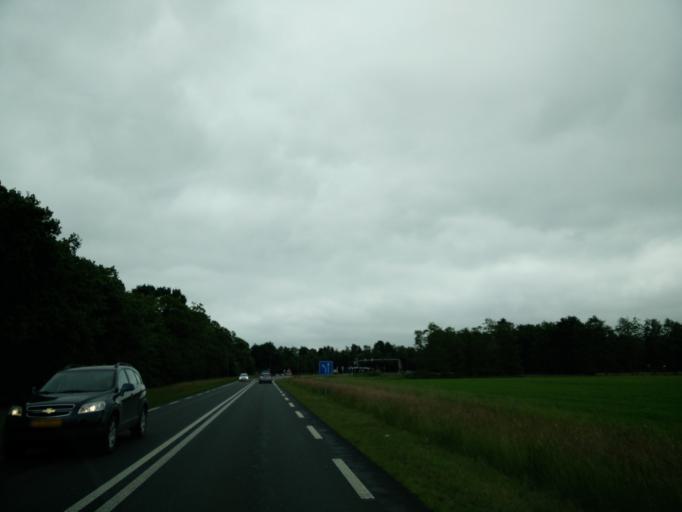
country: NL
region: Groningen
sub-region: Gemeente Groningen
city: Groningen
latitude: 53.1509
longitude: 6.4848
